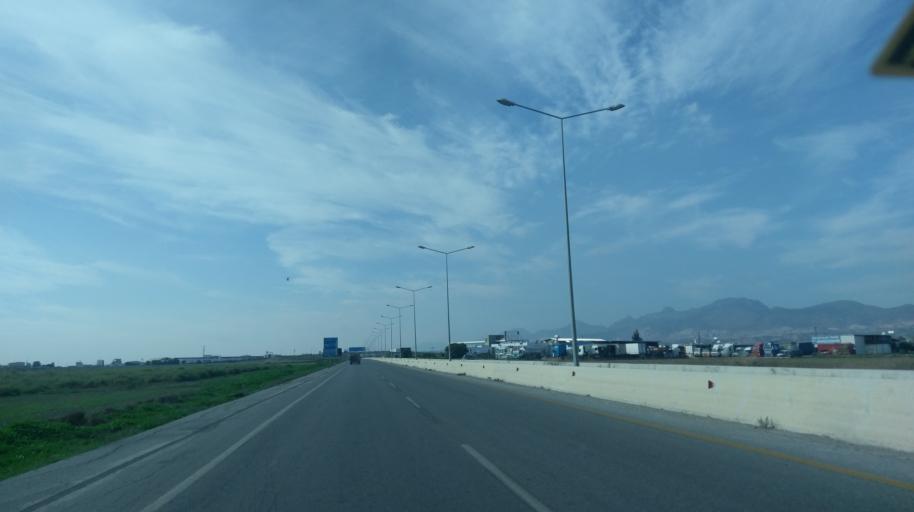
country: CY
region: Lefkosia
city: Geri
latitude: 35.2167
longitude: 33.5065
